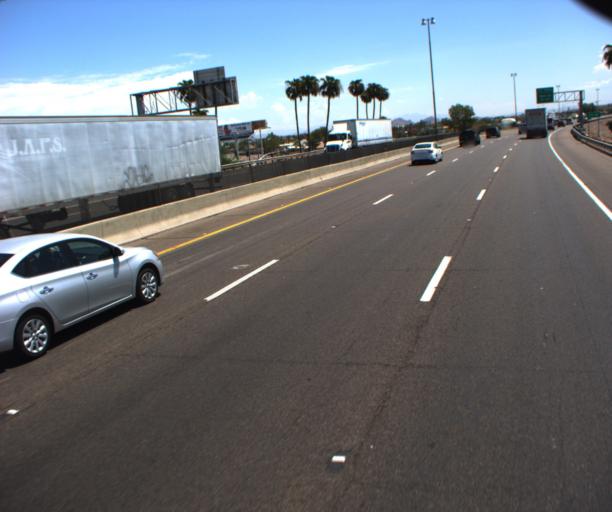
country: US
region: Arizona
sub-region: Maricopa County
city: Phoenix
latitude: 33.4286
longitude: -112.0662
